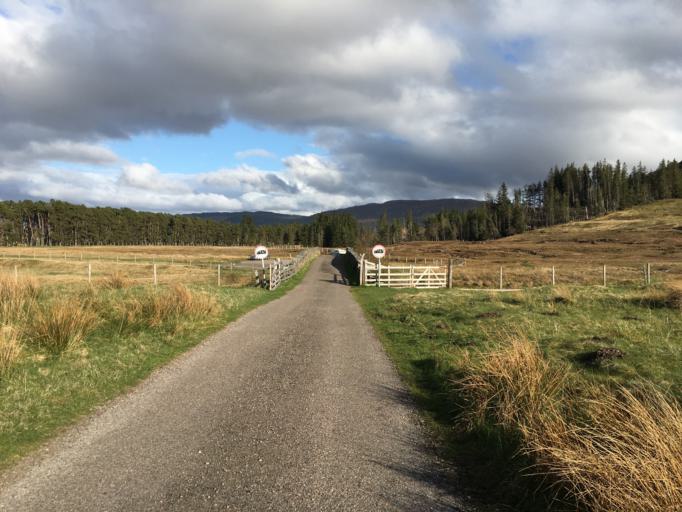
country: GB
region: Scotland
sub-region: Highland
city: Kingussie
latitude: 57.0204
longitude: -4.4373
